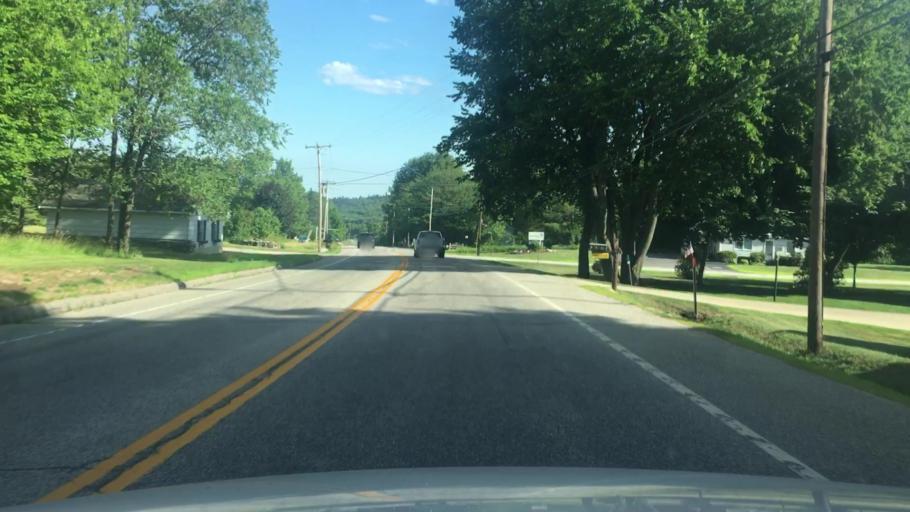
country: US
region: Maine
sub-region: Franklin County
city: Jay
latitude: 44.5139
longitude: -70.2226
